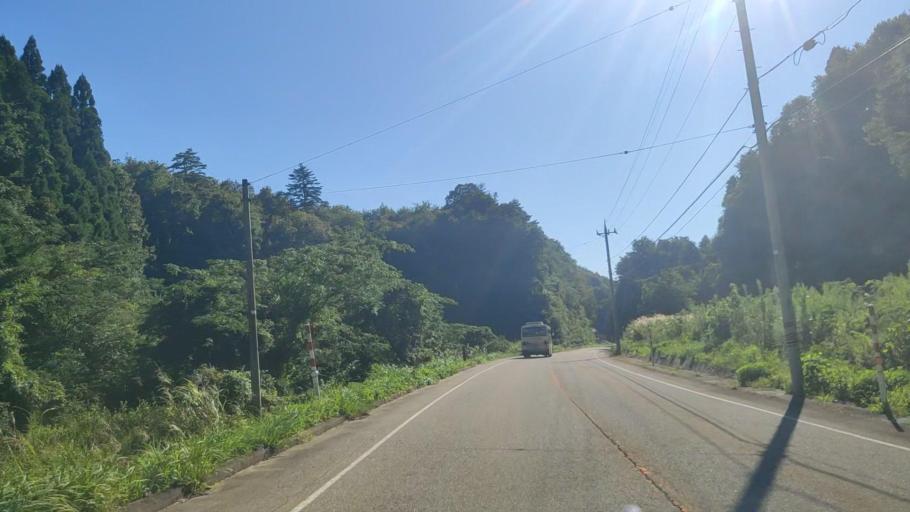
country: JP
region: Ishikawa
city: Nanao
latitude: 37.2470
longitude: 136.9935
